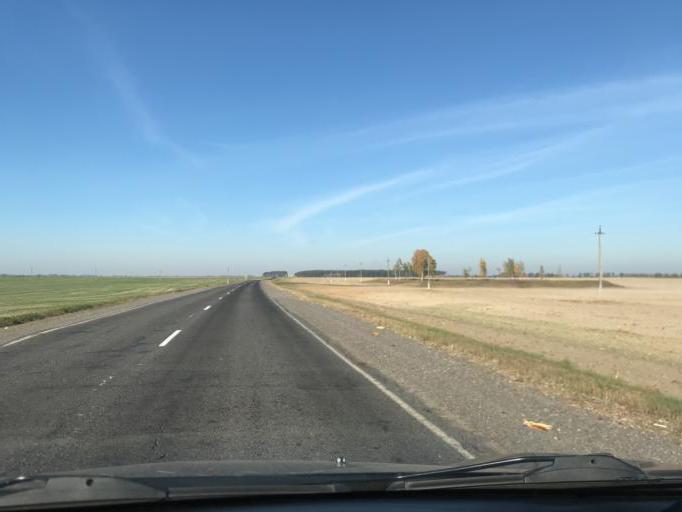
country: BY
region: Gomel
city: Brahin
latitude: 51.8016
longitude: 30.1257
